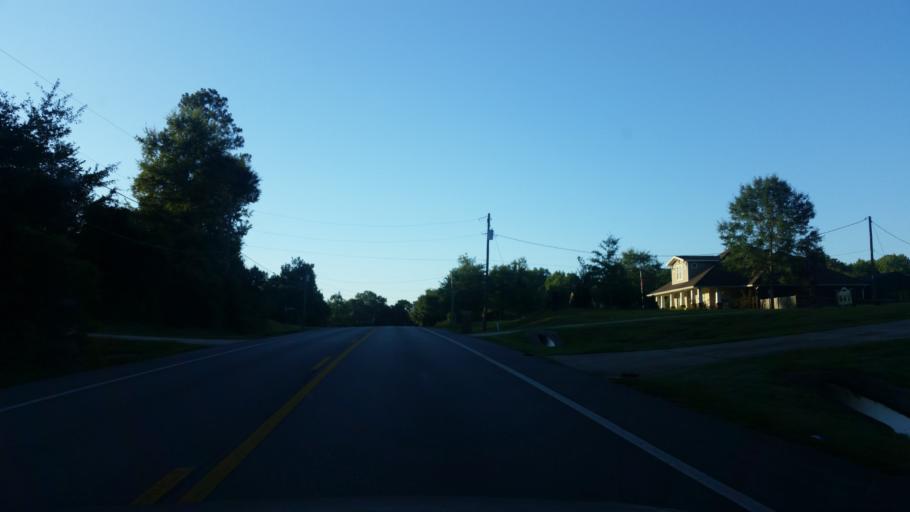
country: US
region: Florida
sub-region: Escambia County
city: Cantonment
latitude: 30.5989
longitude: -87.3527
